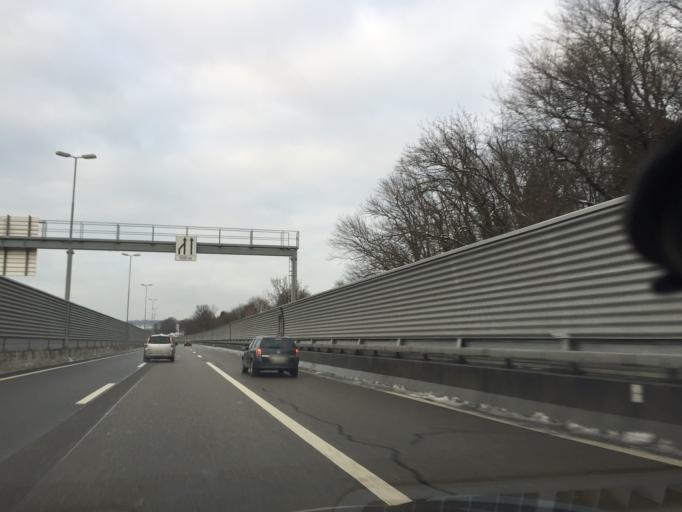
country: CH
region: Zurich
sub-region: Bezirk Zuerich
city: Zuerich (Kreis 2) / Enge
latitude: 47.3549
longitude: 8.5247
